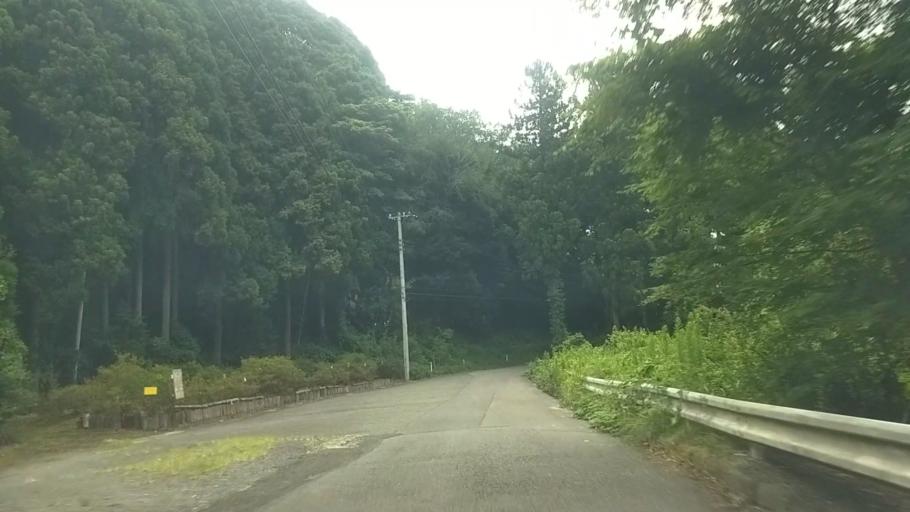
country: JP
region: Chiba
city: Kawaguchi
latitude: 35.1811
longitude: 140.1313
